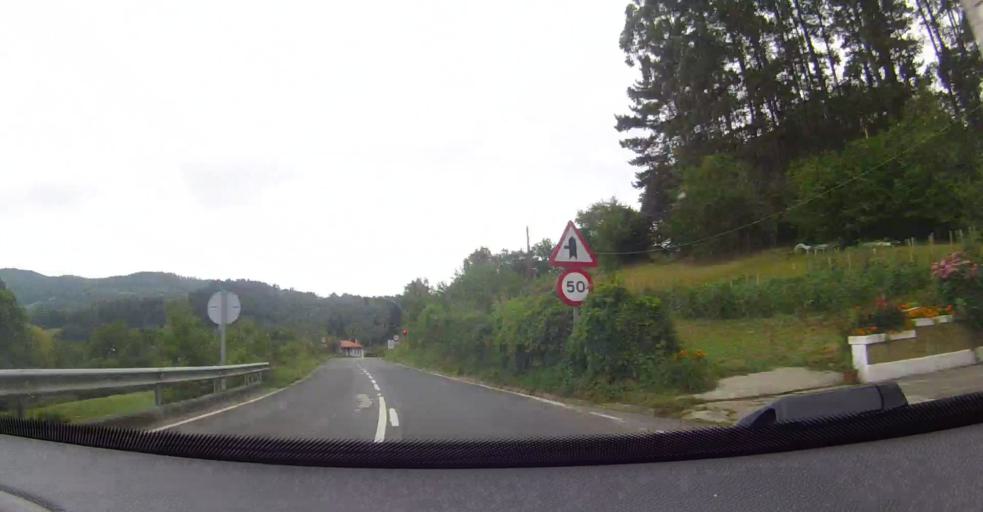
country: ES
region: Basque Country
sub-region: Bizkaia
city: Balmaseda
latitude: 43.2404
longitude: -3.2200
